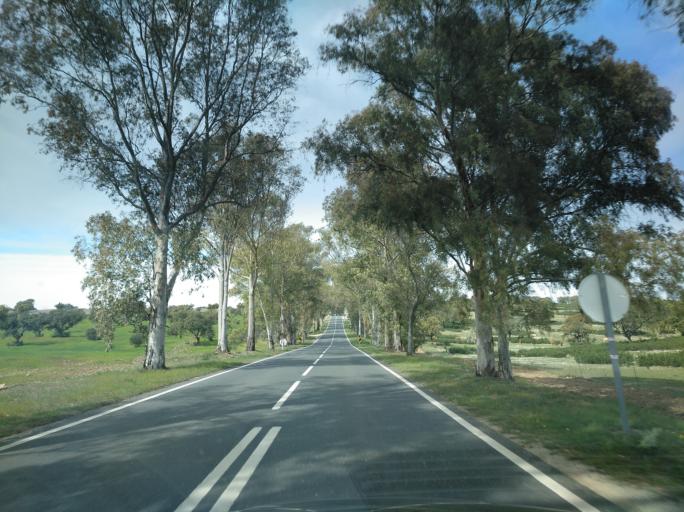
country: PT
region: Beja
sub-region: Mertola
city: Mertola
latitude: 37.7245
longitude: -7.7636
